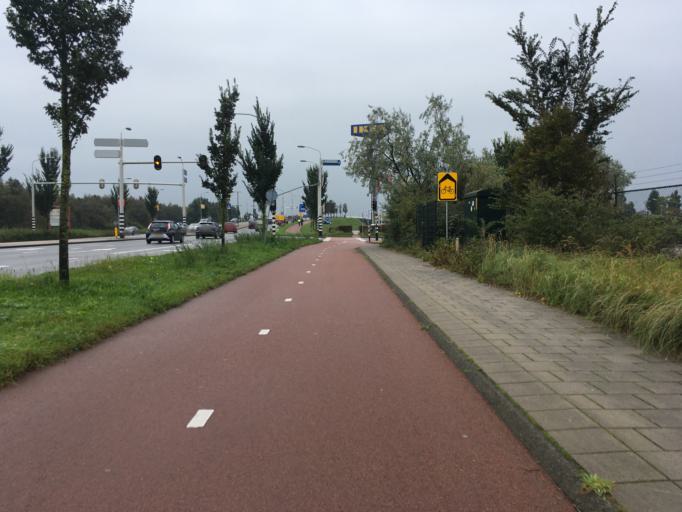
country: NL
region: North Holland
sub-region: Gemeente Haarlem
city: Haarlem
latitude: 52.3863
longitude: 4.6715
